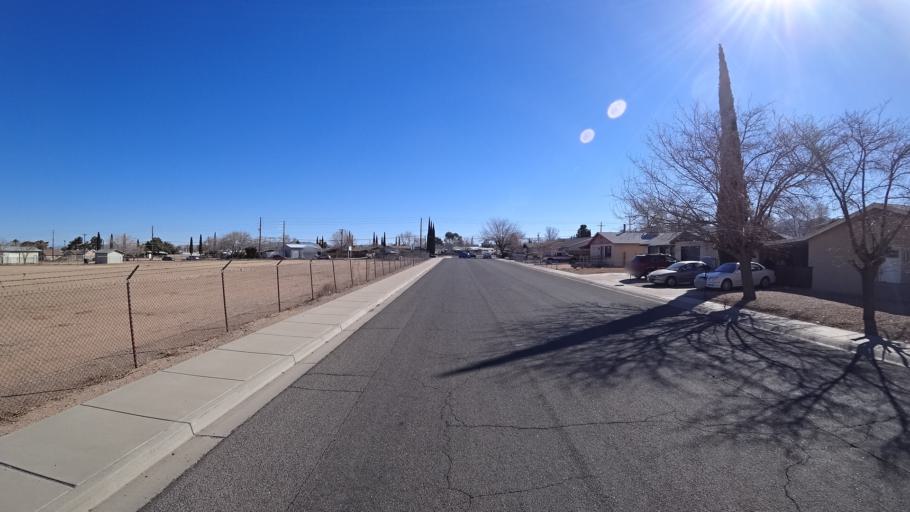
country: US
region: Arizona
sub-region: Mohave County
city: Kingman
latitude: 35.2089
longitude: -114.0260
